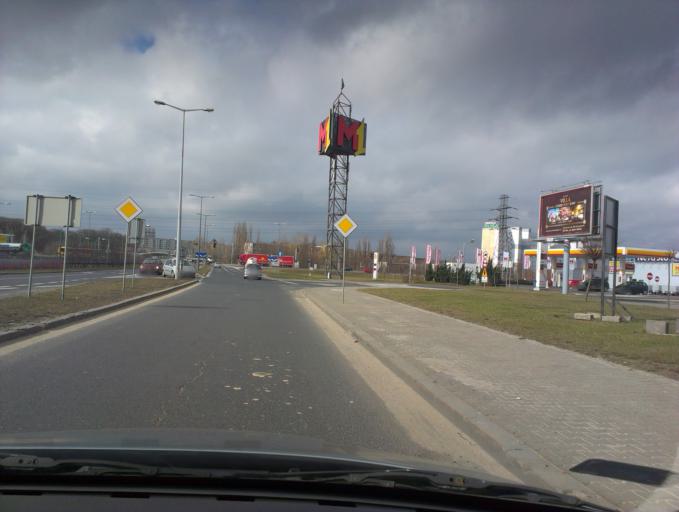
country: PL
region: Greater Poland Voivodeship
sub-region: Poznan
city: Poznan
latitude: 52.3831
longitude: 16.9902
